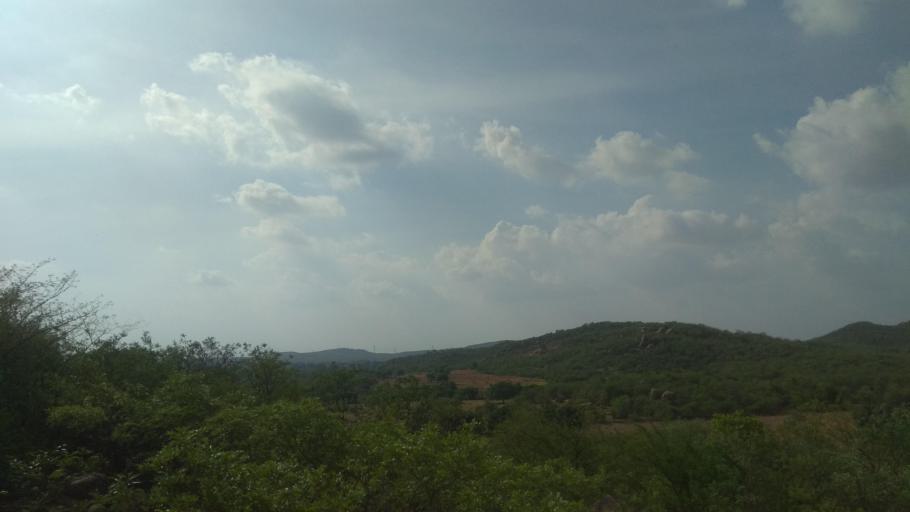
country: IN
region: Telangana
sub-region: Mahbubnagar
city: Farrukhnagar
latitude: 16.8906
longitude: 78.4815
